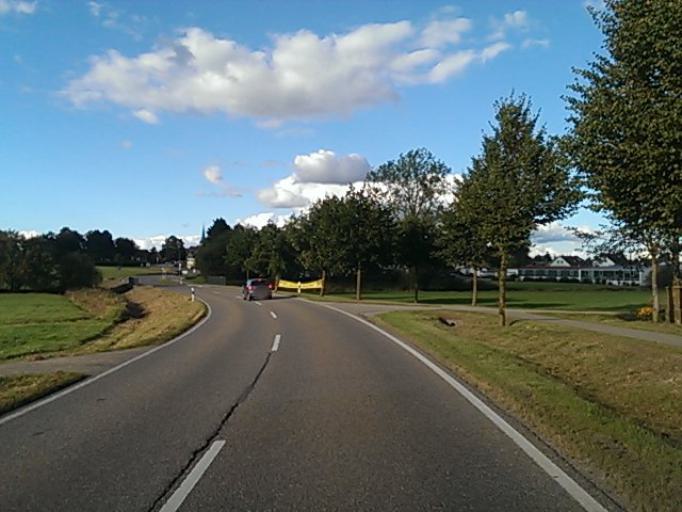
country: DE
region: Baden-Wuerttemberg
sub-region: Freiburg Region
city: Seedorf
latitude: 48.2794
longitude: 8.4890
